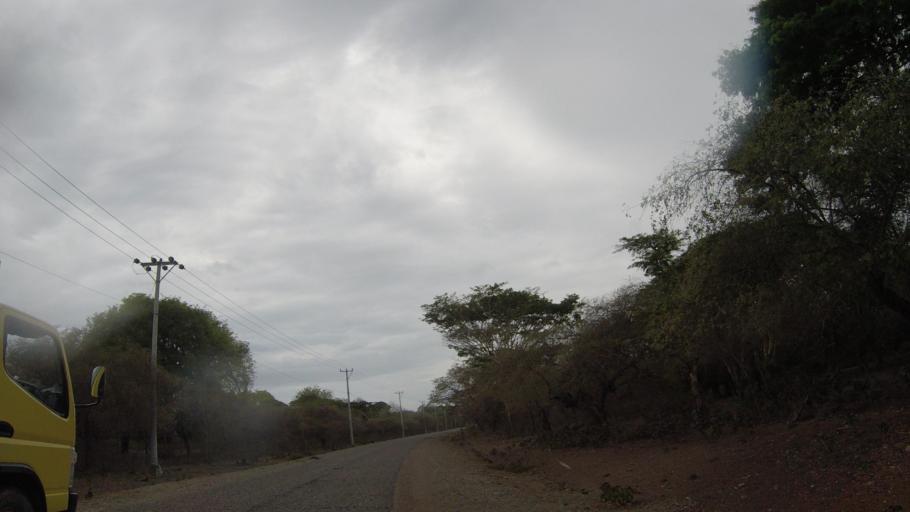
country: TL
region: Lautem
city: Lospalos
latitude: -8.3268
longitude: 126.9843
